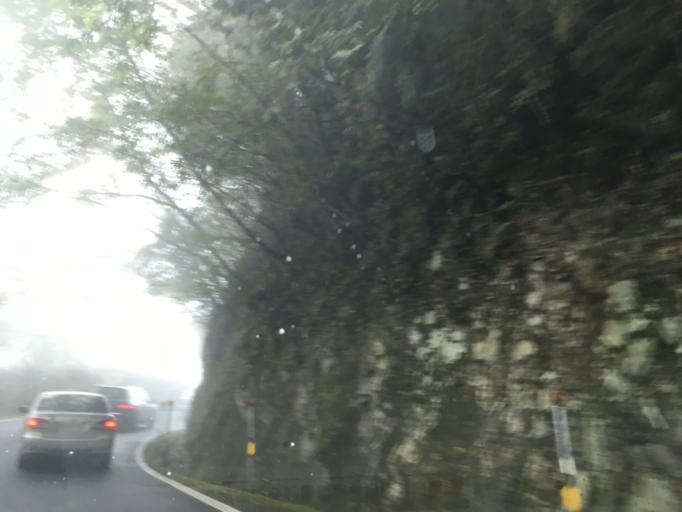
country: TW
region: Taiwan
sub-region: Hualien
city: Hualian
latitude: 24.1870
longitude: 121.4141
